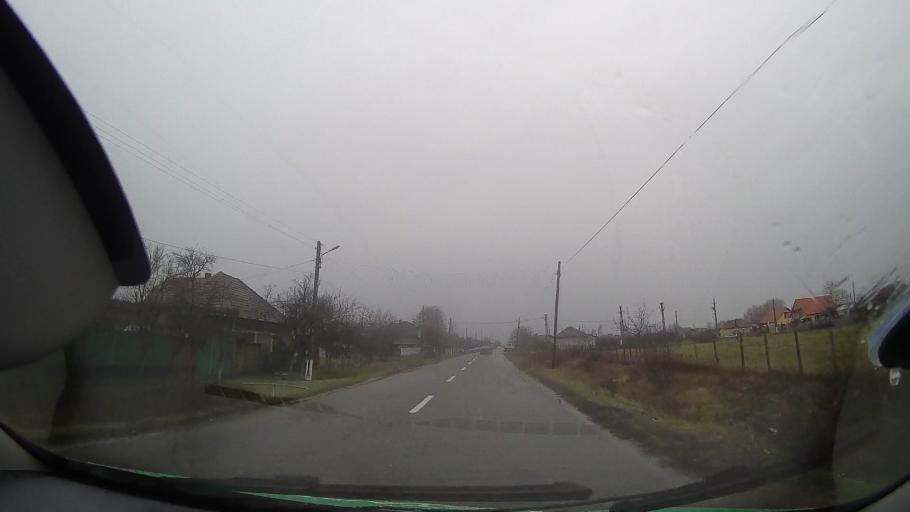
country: RO
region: Bihor
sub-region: Comuna Tulca
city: Tulca
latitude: 46.7935
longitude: 21.7474
